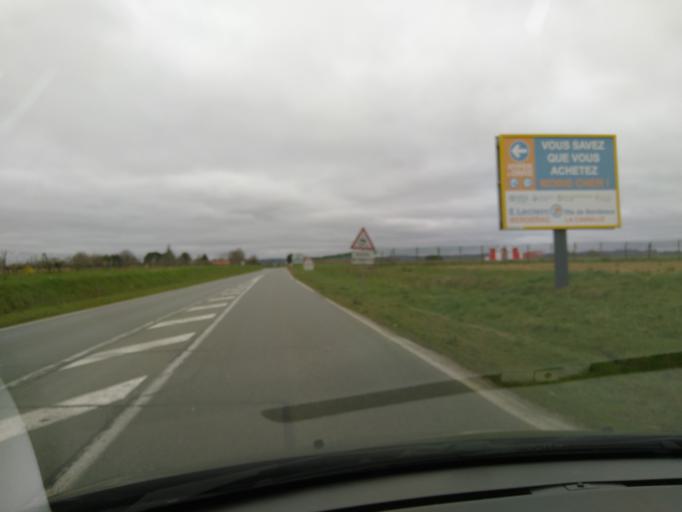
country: FR
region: Aquitaine
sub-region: Departement de la Dordogne
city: Monbazillac
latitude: 44.8239
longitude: 0.5031
